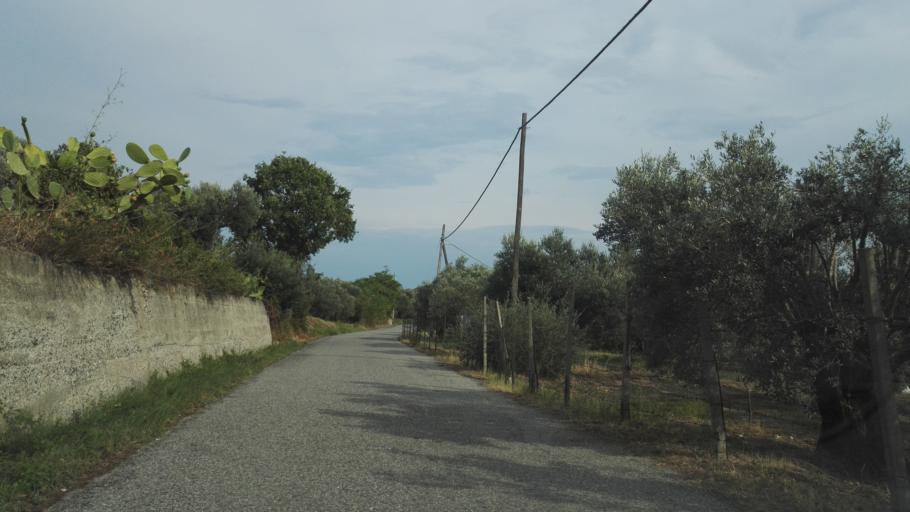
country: IT
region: Calabria
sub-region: Provincia di Reggio Calabria
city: Stignano
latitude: 38.4265
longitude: 16.4637
